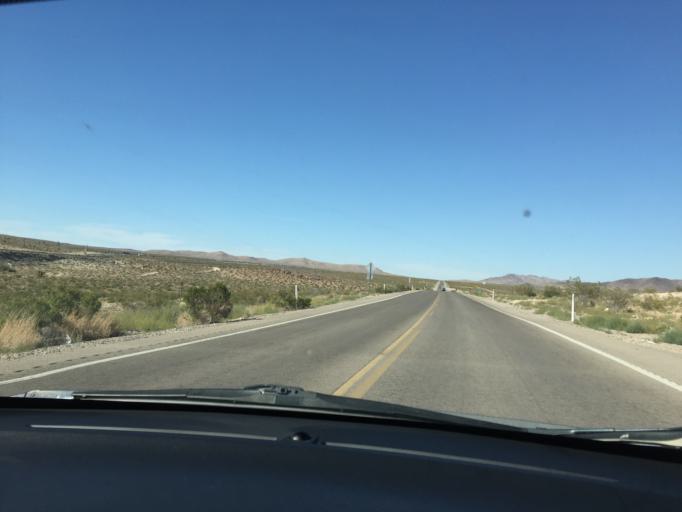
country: US
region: Nevada
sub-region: Clark County
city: Enterprise
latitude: 35.8236
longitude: -115.2881
